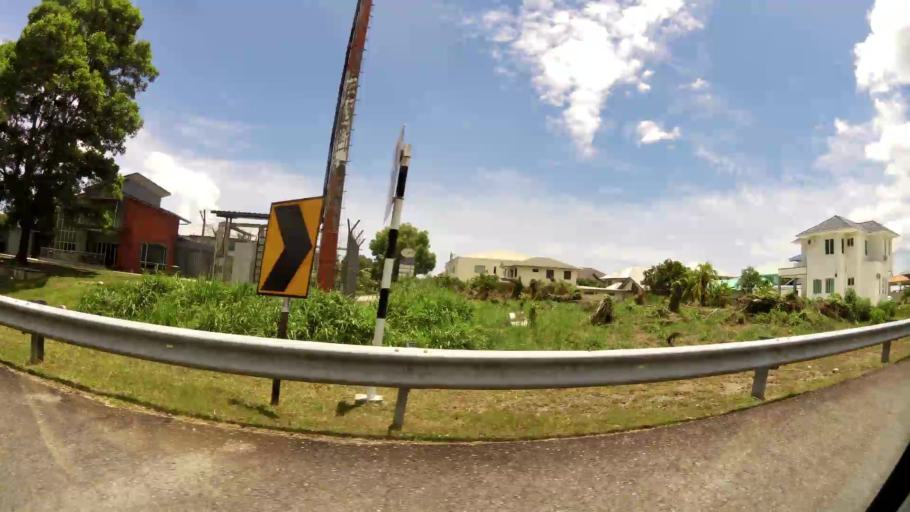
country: BN
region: Brunei and Muara
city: Bandar Seri Begawan
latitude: 4.9447
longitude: 114.9094
